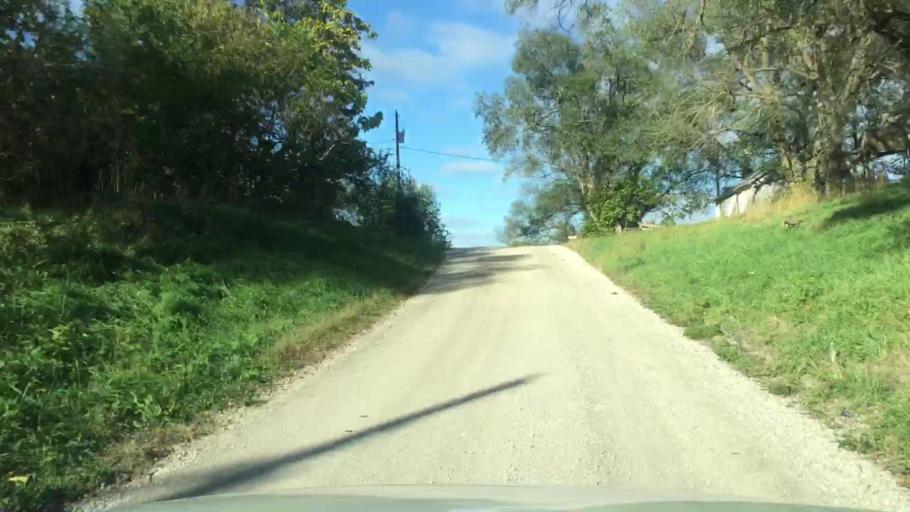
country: US
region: Missouri
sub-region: Howard County
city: New Franklin
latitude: 39.0835
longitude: -92.7761
